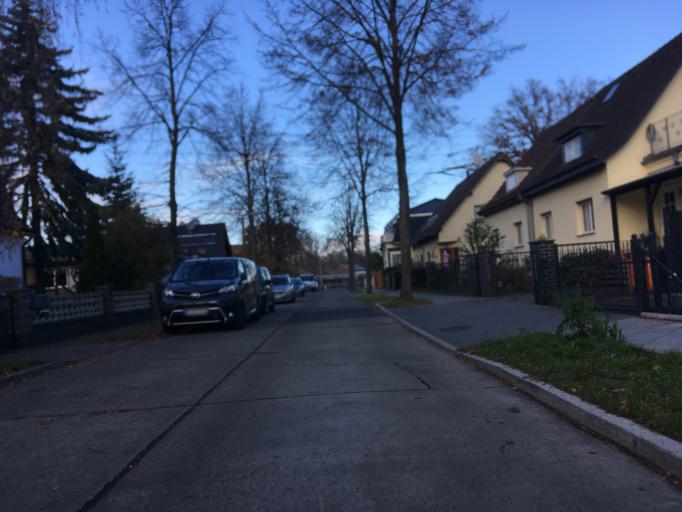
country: DE
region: Berlin
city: Karlshorst
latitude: 52.4950
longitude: 13.5317
